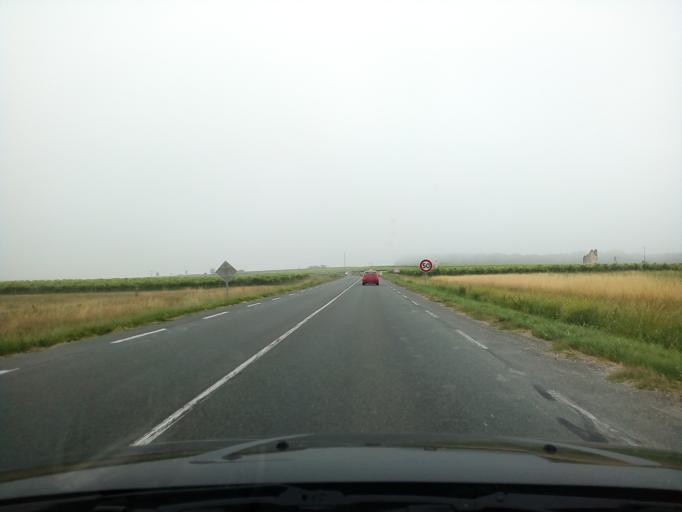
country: FR
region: Poitou-Charentes
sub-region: Departement de la Charente-Maritime
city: Cherac
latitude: 45.6916
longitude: -0.4102
